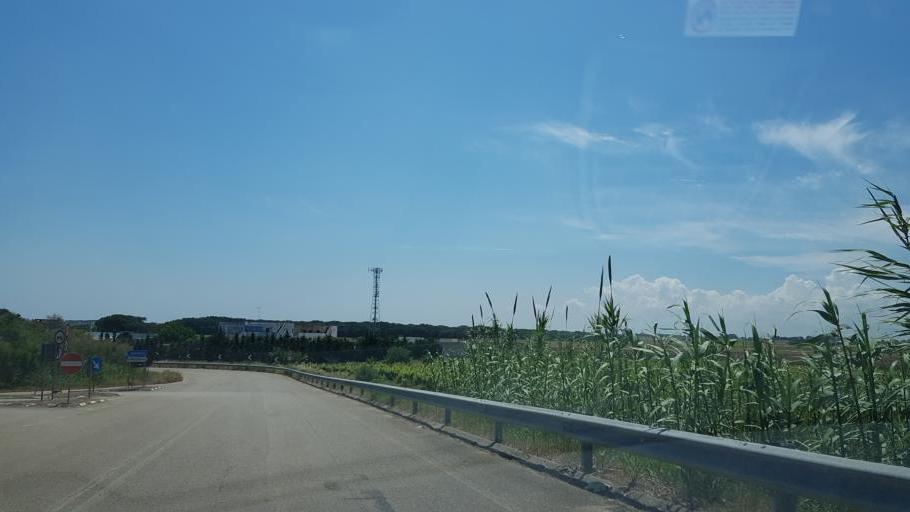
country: IT
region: Apulia
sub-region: Provincia di Brindisi
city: Brindisi
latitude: 40.6646
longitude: 17.8758
